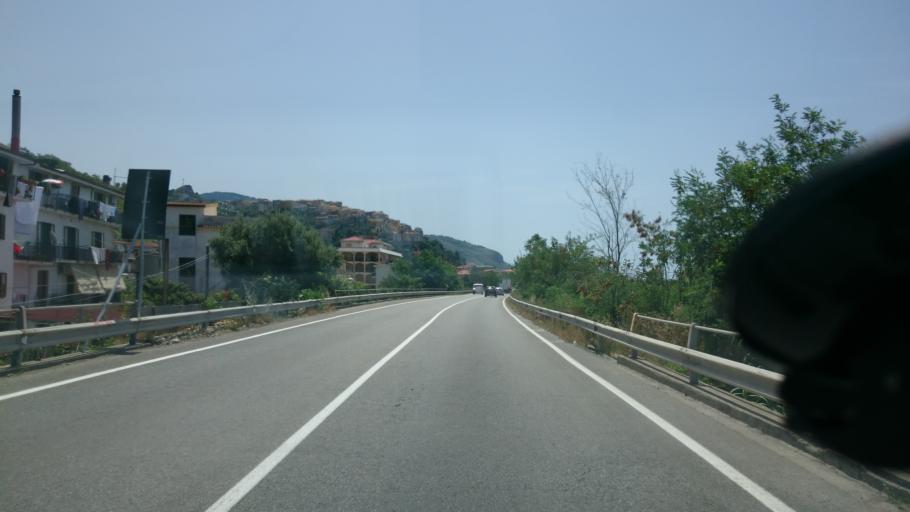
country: IT
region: Calabria
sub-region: Provincia di Cosenza
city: Cetraro Marina
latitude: 39.5256
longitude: 15.9288
